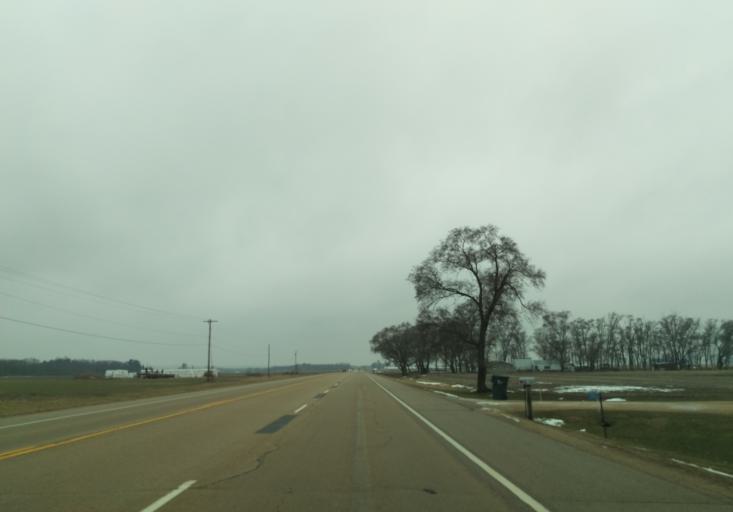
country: US
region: Wisconsin
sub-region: Sauk County
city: Spring Green
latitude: 43.1899
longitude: -90.1007
